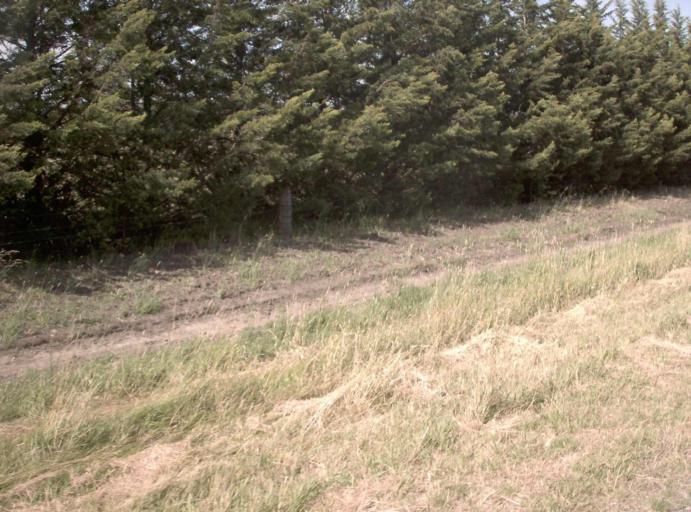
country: AU
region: Victoria
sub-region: Wellington
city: Heyfield
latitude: -38.1544
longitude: 146.8039
